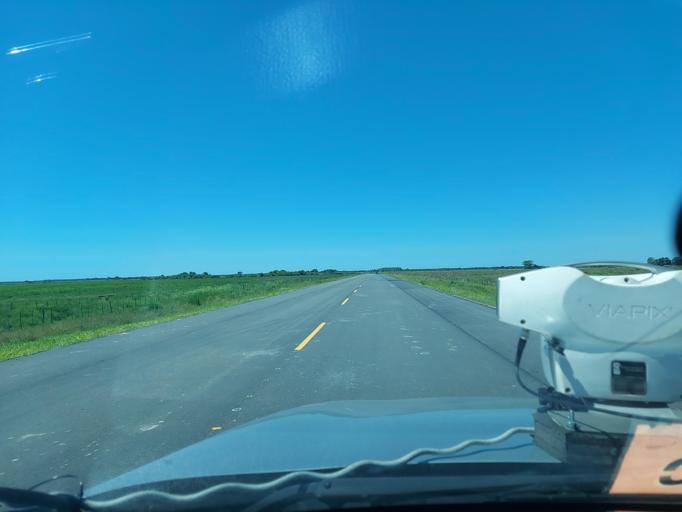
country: PY
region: Neembucu
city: Pilar
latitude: -26.8413
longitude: -58.2298
